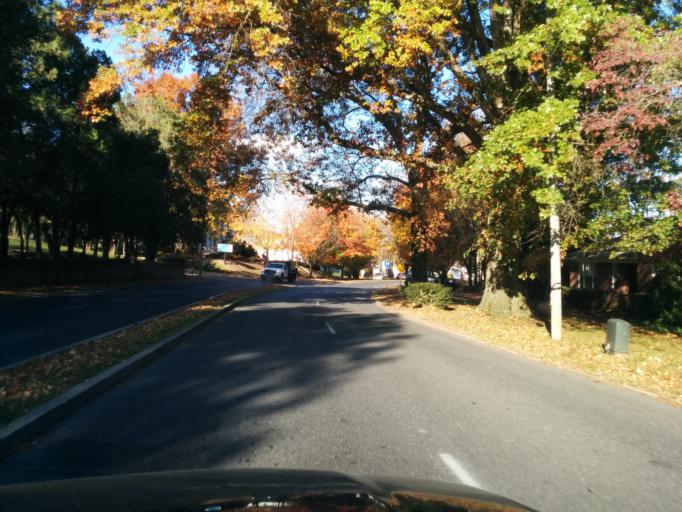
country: US
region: Virginia
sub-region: City of Lexington
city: Lexington
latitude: 37.7813
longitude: -79.4385
